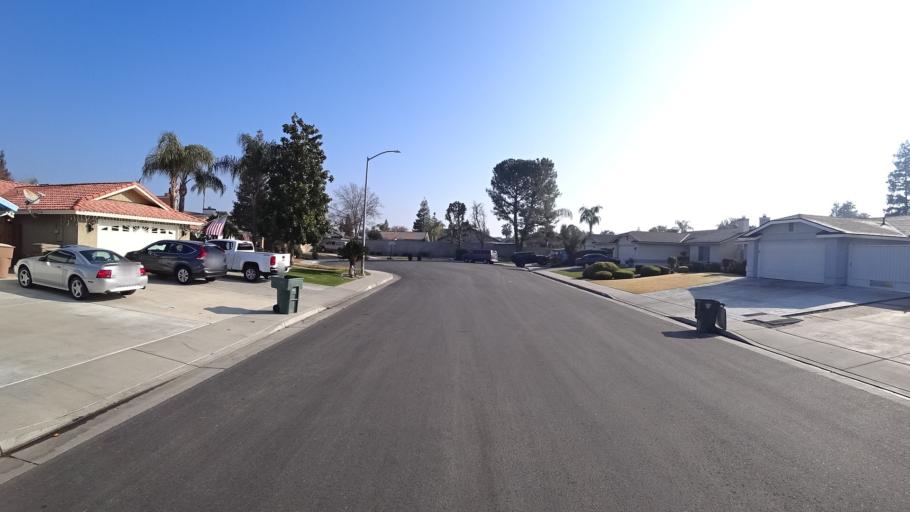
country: US
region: California
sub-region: Kern County
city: Greenacres
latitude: 35.3891
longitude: -119.1052
